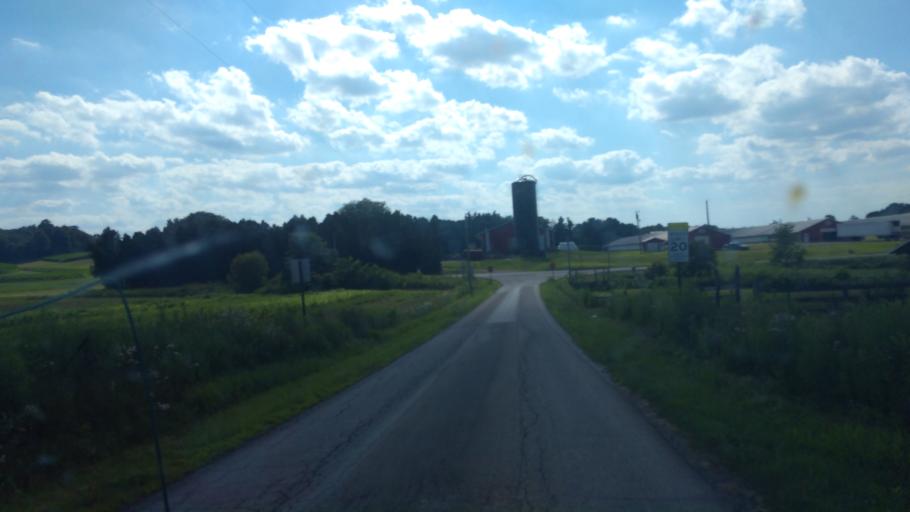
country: US
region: Ohio
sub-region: Wayne County
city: Dalton
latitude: 40.7535
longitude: -81.6897
